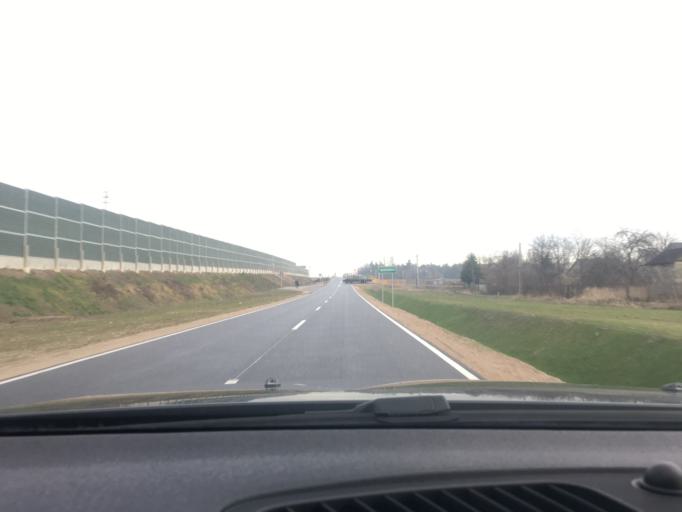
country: PL
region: Swietokrzyskie
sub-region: Powiat jedrzejowski
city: Jedrzejow
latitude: 50.6666
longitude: 20.3389
